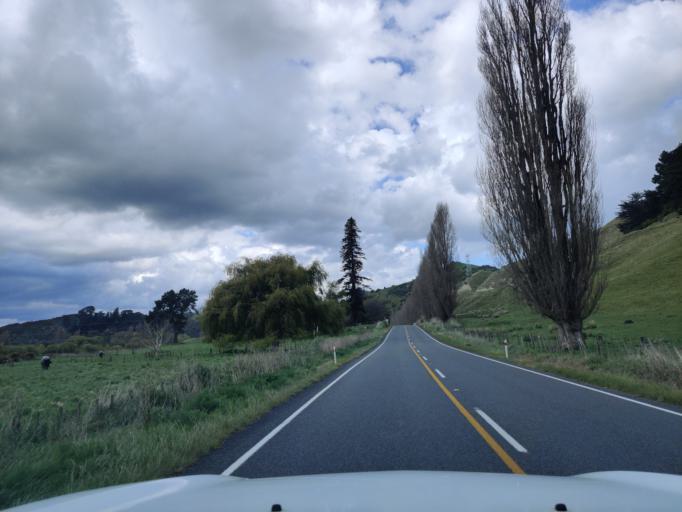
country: NZ
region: Manawatu-Wanganui
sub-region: Wanganui District
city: Wanganui
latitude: -39.8965
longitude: 175.0956
